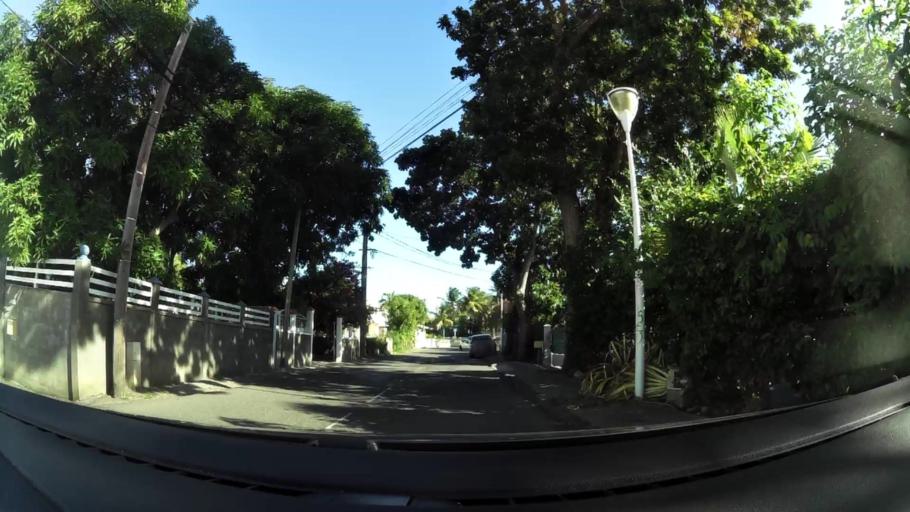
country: GP
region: Guadeloupe
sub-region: Guadeloupe
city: Le Gosier
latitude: 16.2047
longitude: -61.4800
